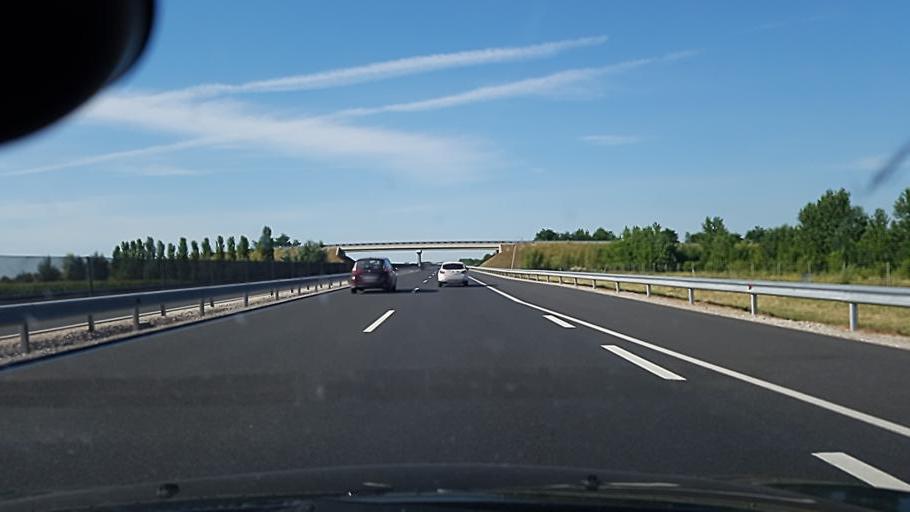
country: HU
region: Tolna
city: Dunaszentgyorgy
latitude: 46.5423
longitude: 18.7868
